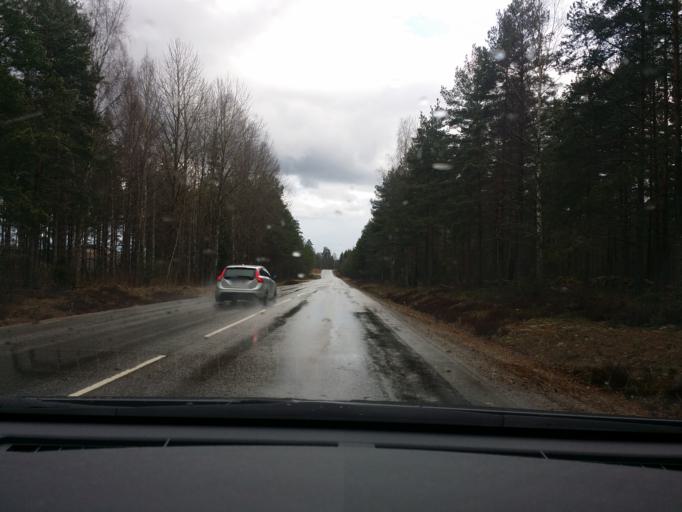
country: SE
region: Soedermanland
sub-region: Eskilstuna Kommun
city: Arla
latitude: 59.3458
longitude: 16.6912
